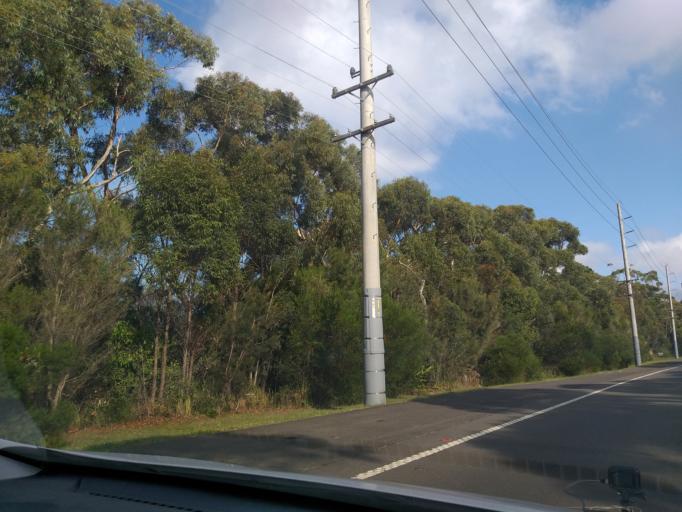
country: AU
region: New South Wales
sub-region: Wollongong
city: Helensburgh
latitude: -34.1989
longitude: 150.9704
